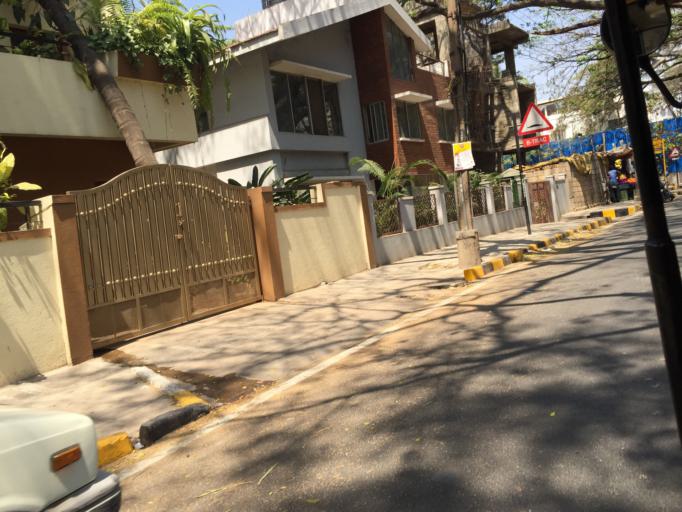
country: IN
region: Karnataka
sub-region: Bangalore Urban
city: Bangalore
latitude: 12.9796
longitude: 77.6369
